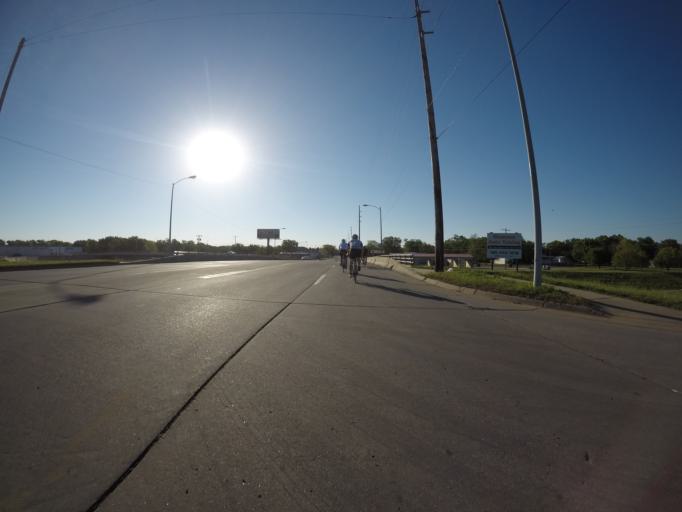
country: US
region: Kansas
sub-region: Shawnee County
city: Topeka
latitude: 39.0489
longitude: -95.6626
